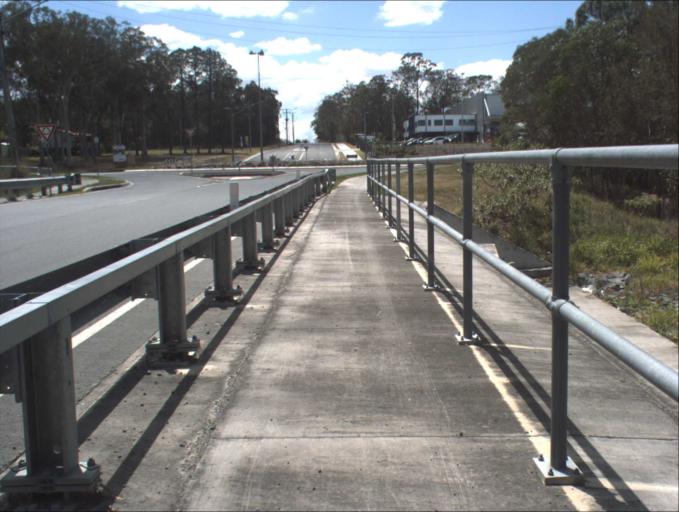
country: AU
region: Queensland
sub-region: Logan
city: Woodridge
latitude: -27.6526
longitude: 153.0873
